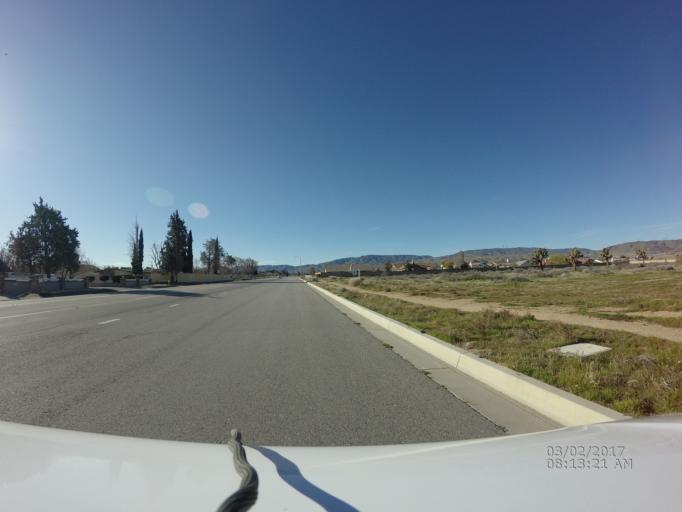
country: US
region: California
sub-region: Los Angeles County
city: Quartz Hill
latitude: 34.6407
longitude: -118.1833
